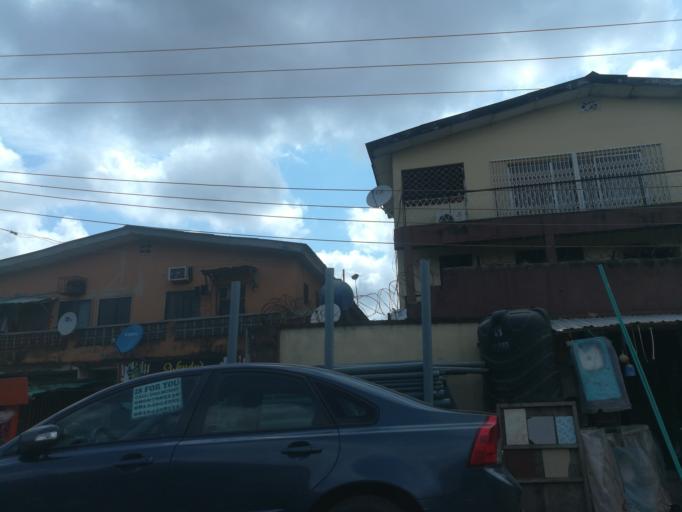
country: NG
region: Lagos
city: Somolu
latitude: 6.5288
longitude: 3.3807
